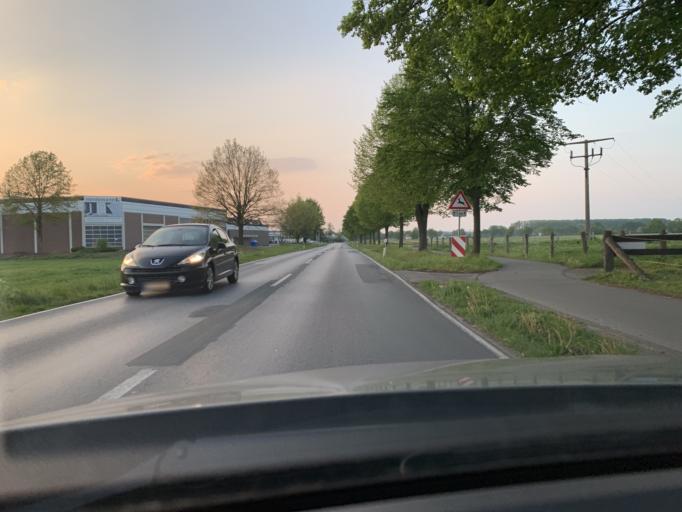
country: DE
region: North Rhine-Westphalia
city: Rietberg
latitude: 51.7599
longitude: 8.3870
